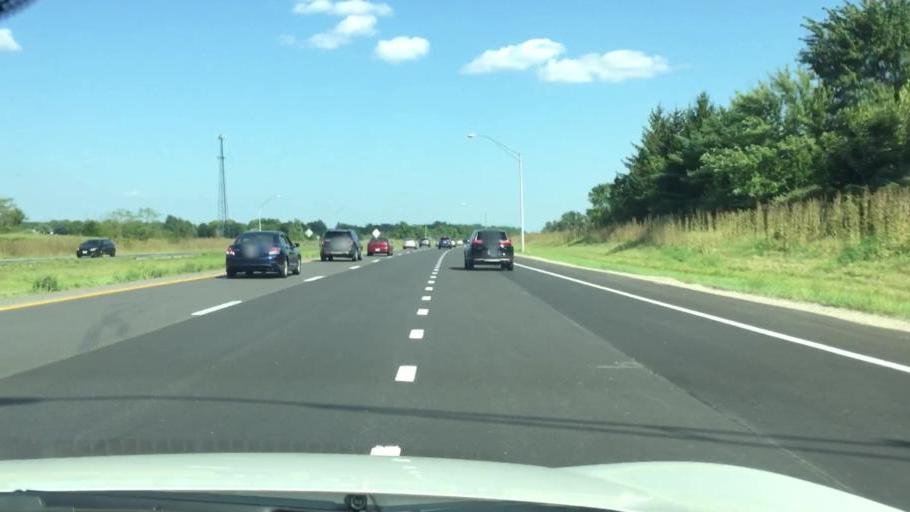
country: US
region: Ohio
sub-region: Champaign County
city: North Lewisburg
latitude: 40.2676
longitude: -83.4977
